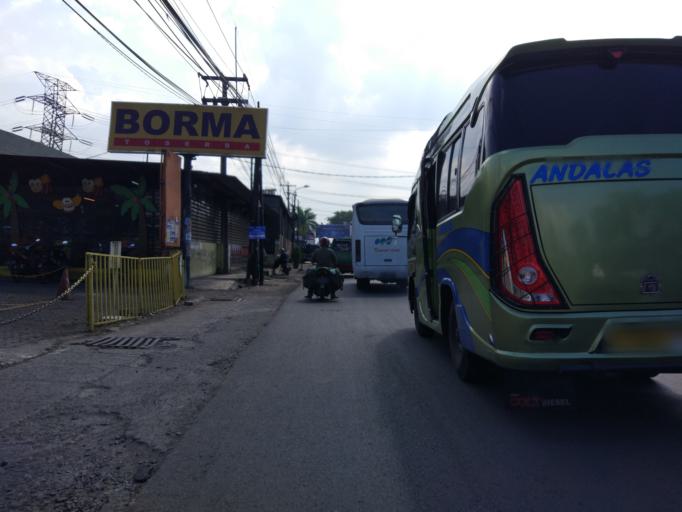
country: ID
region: West Java
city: Cileunyi
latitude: -6.9372
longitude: 107.7312
